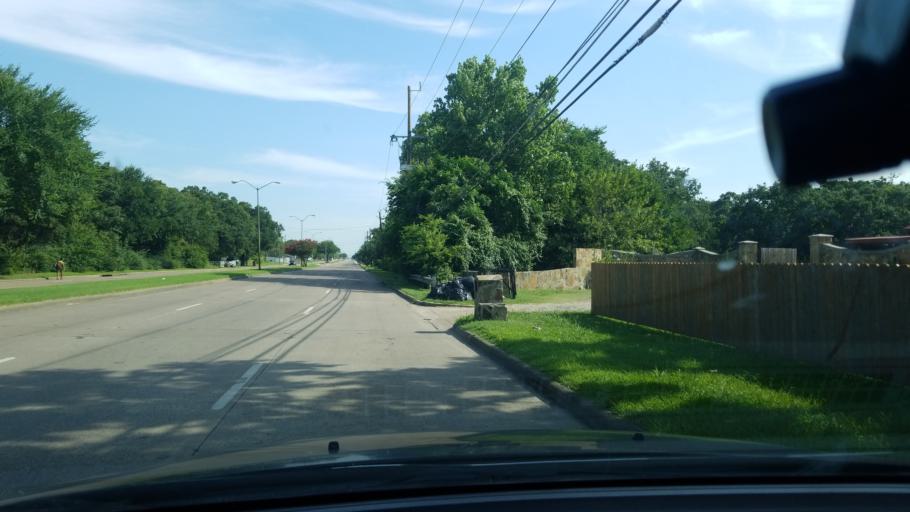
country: US
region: Texas
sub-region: Dallas County
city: Balch Springs
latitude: 32.7203
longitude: -96.6483
